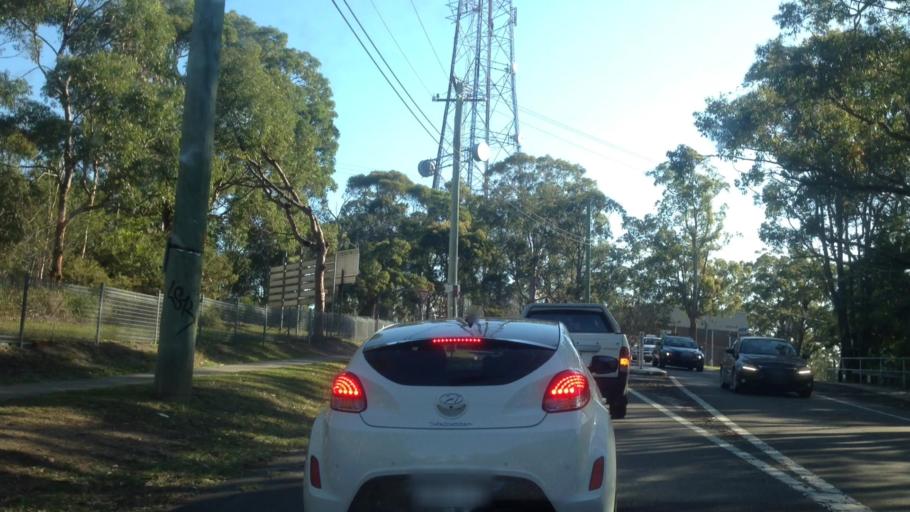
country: AU
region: New South Wales
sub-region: Lake Macquarie Shire
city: Dora Creek
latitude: -33.1132
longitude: 151.5151
